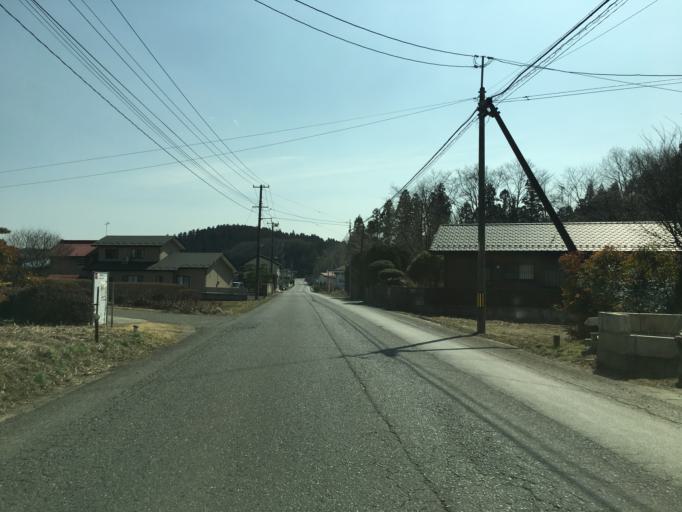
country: JP
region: Fukushima
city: Ishikawa
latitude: 37.1459
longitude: 140.3982
